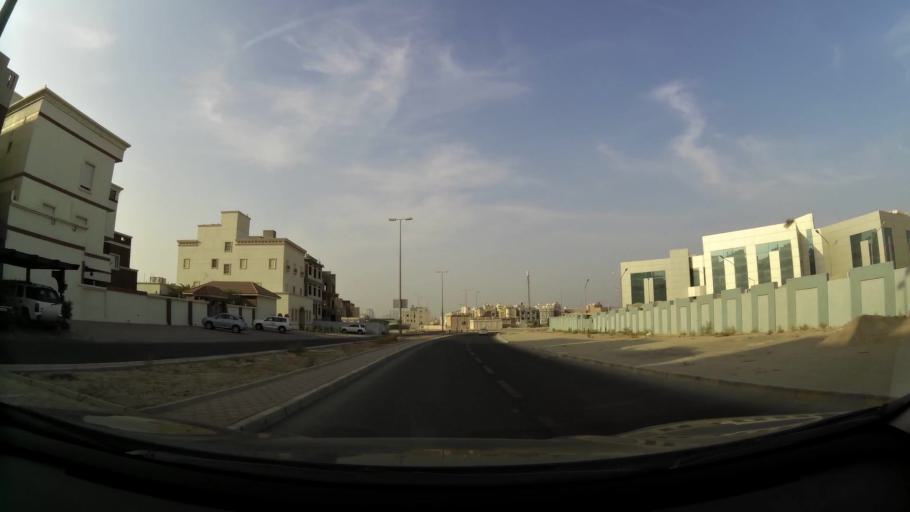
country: KW
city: Al Funaytis
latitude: 29.2293
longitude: 48.0901
